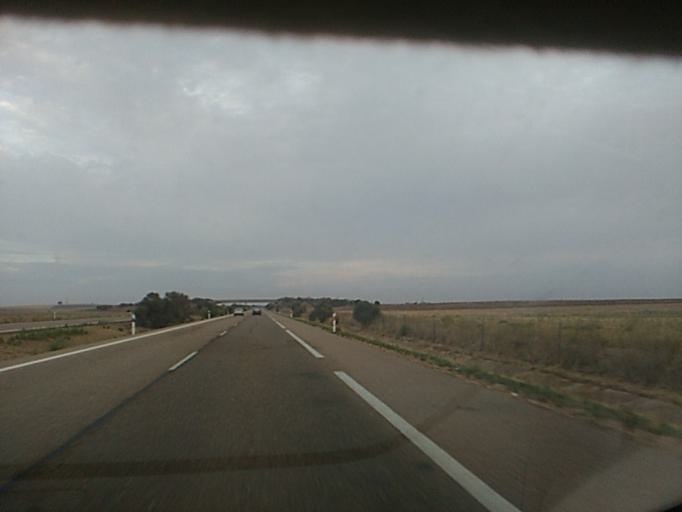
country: ES
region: Castille and Leon
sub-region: Provincia de Valladolid
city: Villardefrades
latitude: 41.7455
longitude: -5.2757
